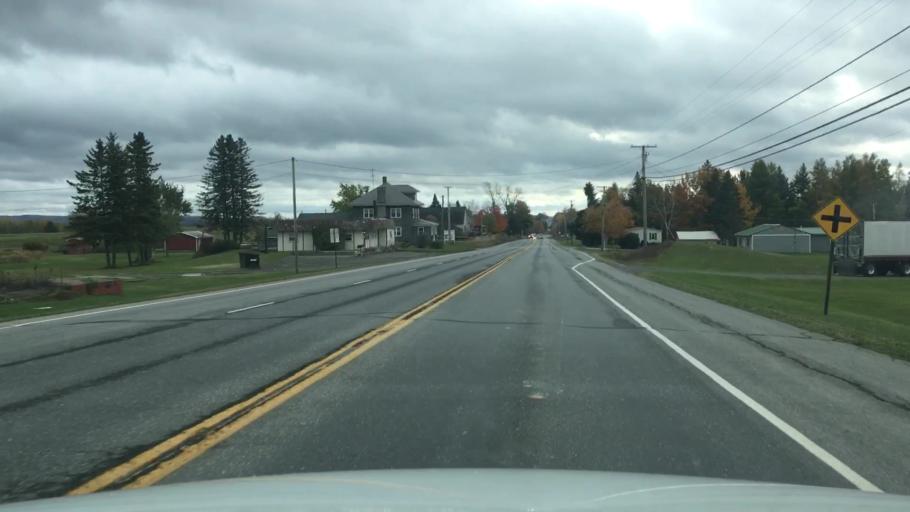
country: US
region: Maine
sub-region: Aroostook County
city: Houlton
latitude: 46.2185
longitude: -67.8410
